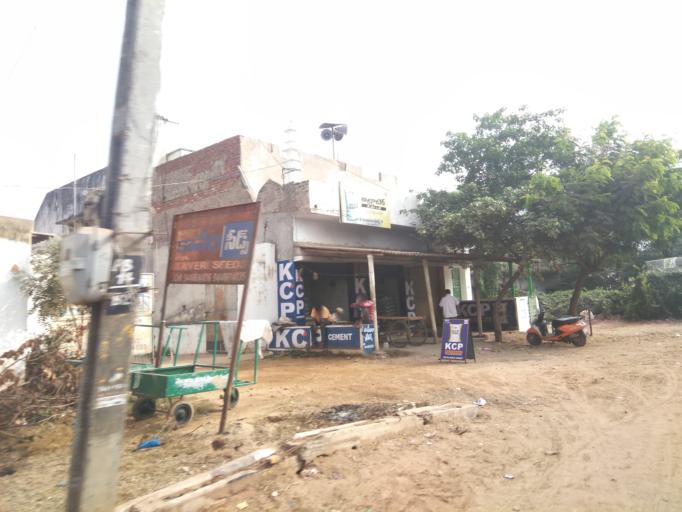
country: IN
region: Andhra Pradesh
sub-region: Nellore
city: Nellore
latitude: 14.4664
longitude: 79.9940
